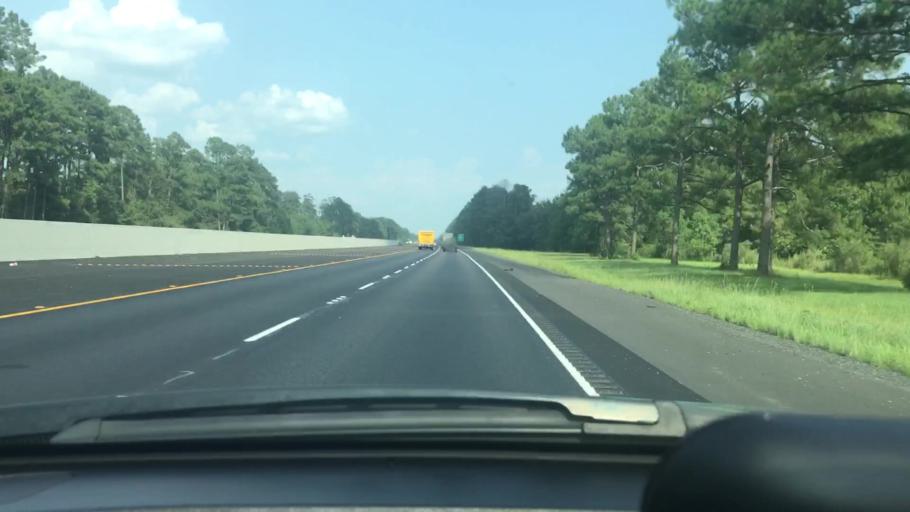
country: US
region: Louisiana
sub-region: Livingston Parish
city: Livingston
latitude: 30.4745
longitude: -90.6675
